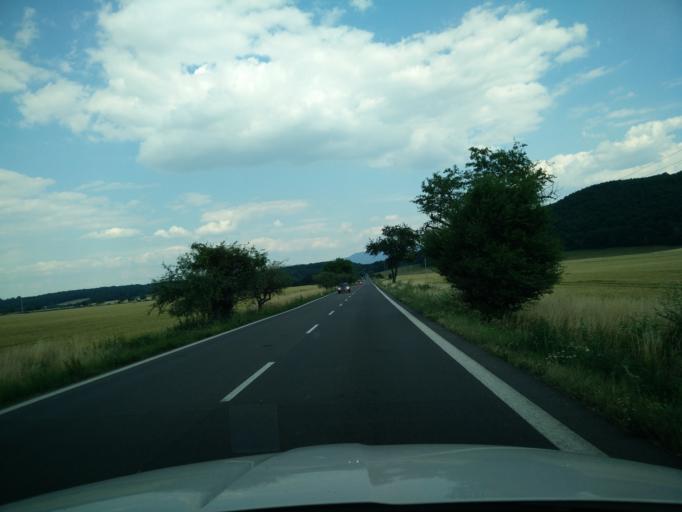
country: SK
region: Nitriansky
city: Novaky
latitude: 48.7231
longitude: 18.4851
